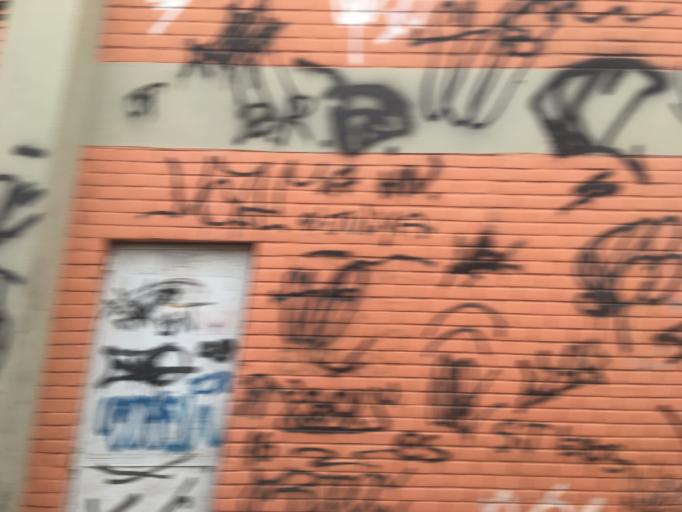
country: BR
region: Rio de Janeiro
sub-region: Rio De Janeiro
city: Rio de Janeiro
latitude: -22.9024
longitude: -43.2661
